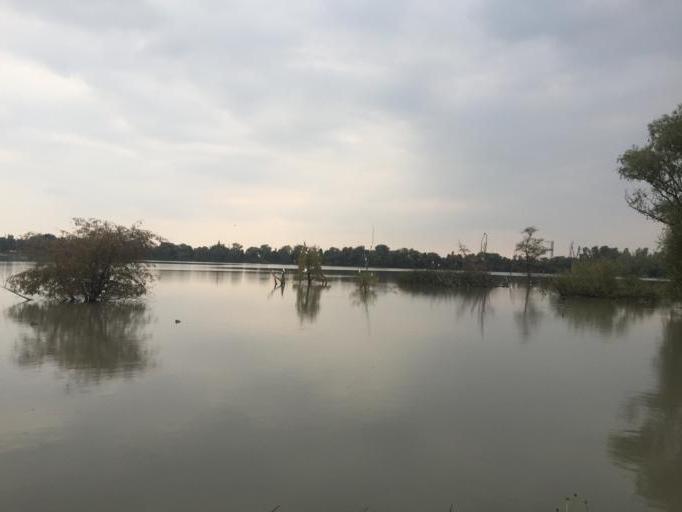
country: MX
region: Mexico
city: Cuautitlan Izcalli
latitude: 19.6509
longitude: -99.2225
